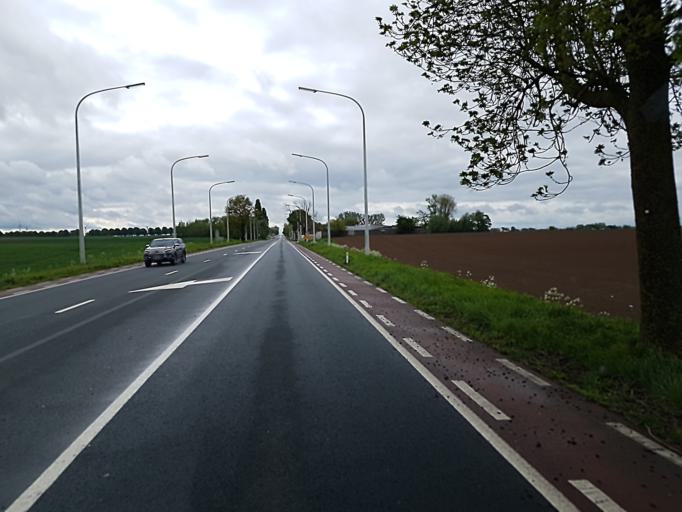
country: BE
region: Wallonia
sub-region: Province du Brabant Wallon
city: Chastre-Villeroux-Blanmont
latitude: 50.6196
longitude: 4.6615
